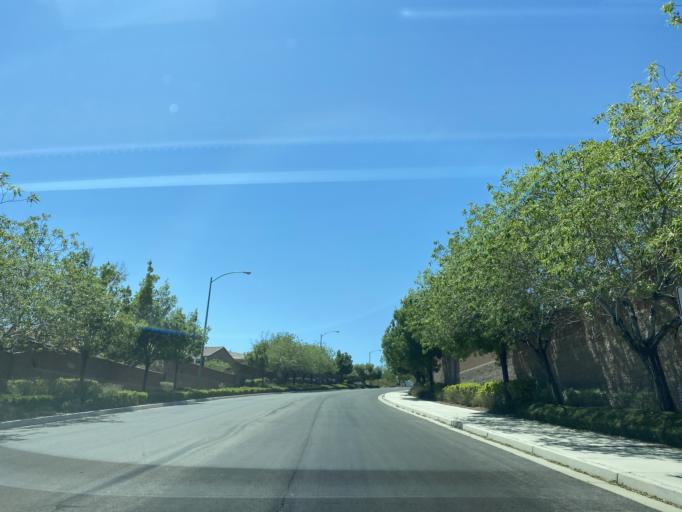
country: US
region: Nevada
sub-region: Clark County
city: Whitney
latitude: 35.9474
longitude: -115.0847
